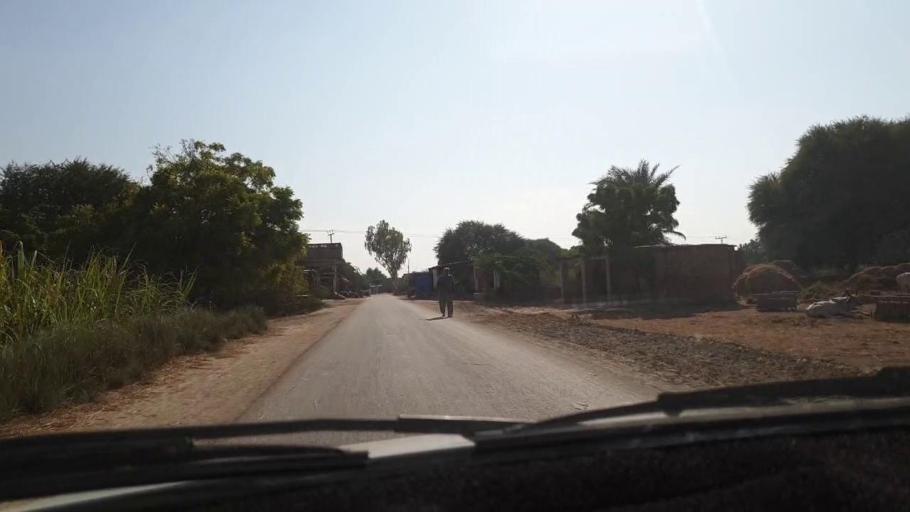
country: PK
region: Sindh
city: Bulri
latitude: 24.9605
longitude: 68.4199
